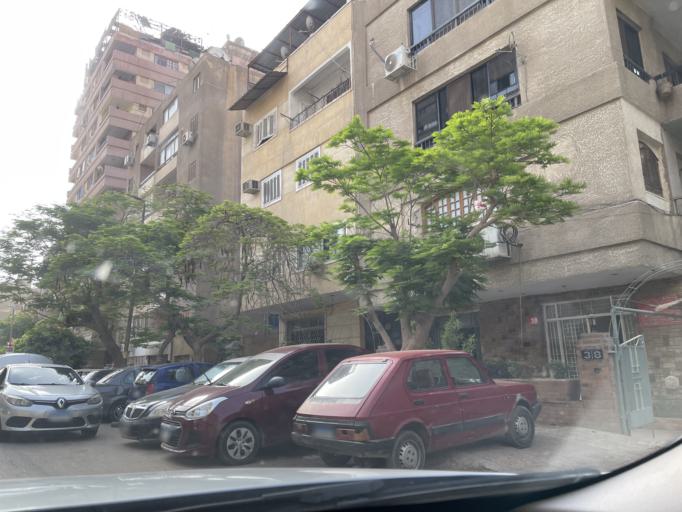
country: EG
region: Muhafazat al Qahirah
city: Cairo
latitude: 30.0662
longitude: 31.3551
